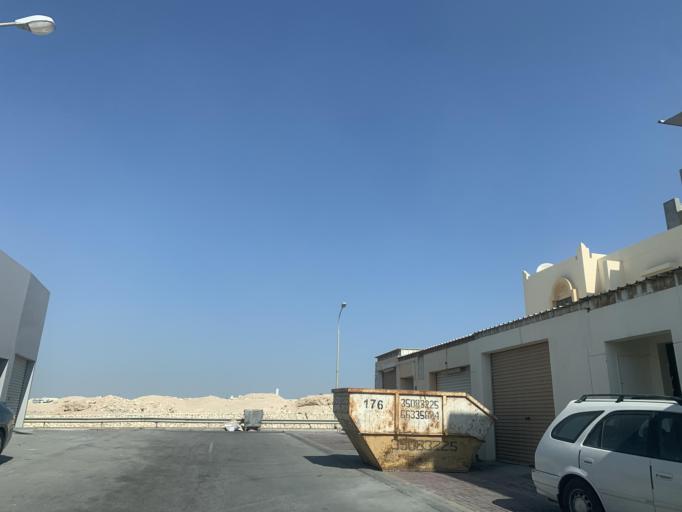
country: BH
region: Central Governorate
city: Madinat Hamad
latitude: 26.1170
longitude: 50.4986
